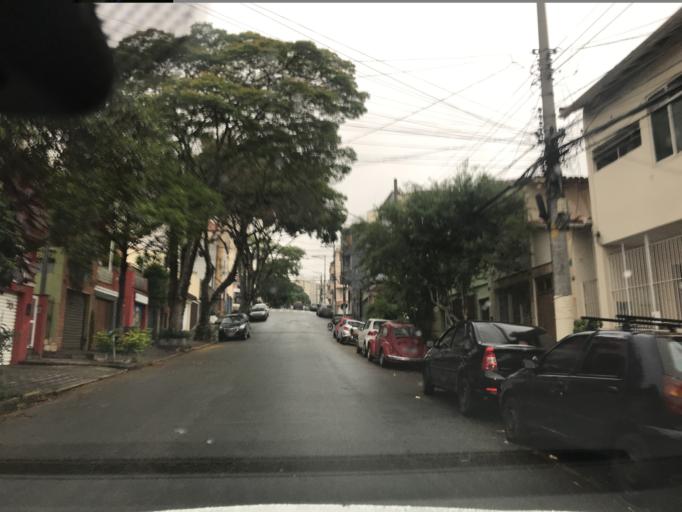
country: BR
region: Sao Paulo
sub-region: Sao Paulo
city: Sao Paulo
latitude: -23.5376
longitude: -46.6873
